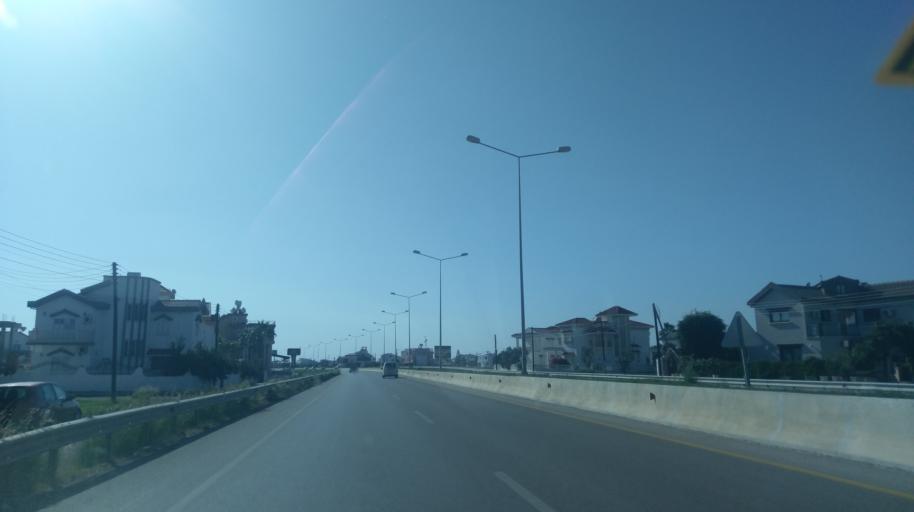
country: CY
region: Ammochostos
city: Trikomo
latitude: 35.2153
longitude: 33.8942
